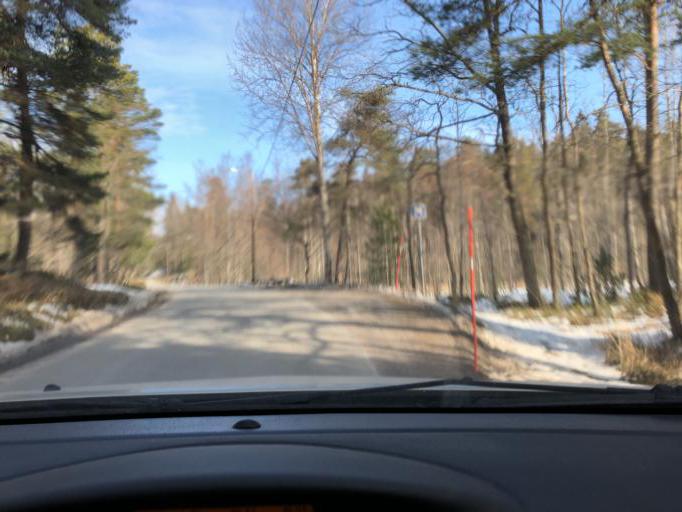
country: SE
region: Stockholm
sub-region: Nacka Kommun
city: Boo
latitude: 59.3369
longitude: 18.3181
